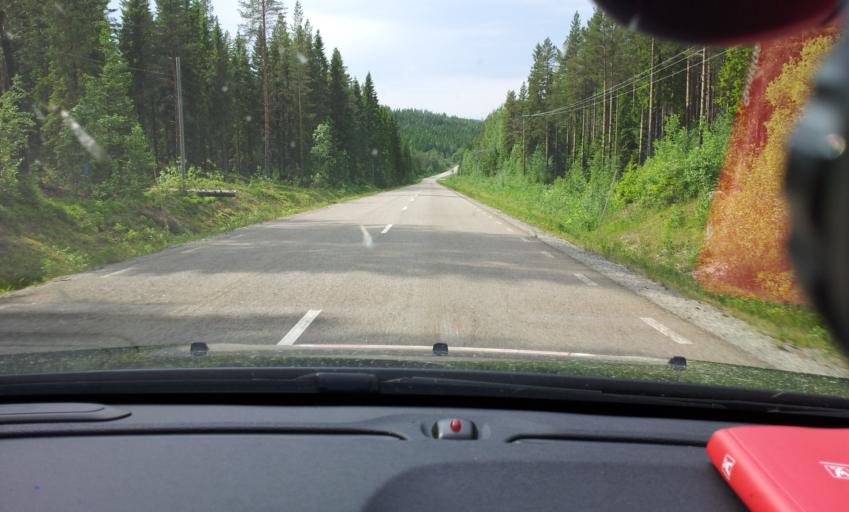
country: SE
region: Jaemtland
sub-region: OEstersunds Kommun
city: Brunflo
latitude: 62.6540
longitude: 14.8892
